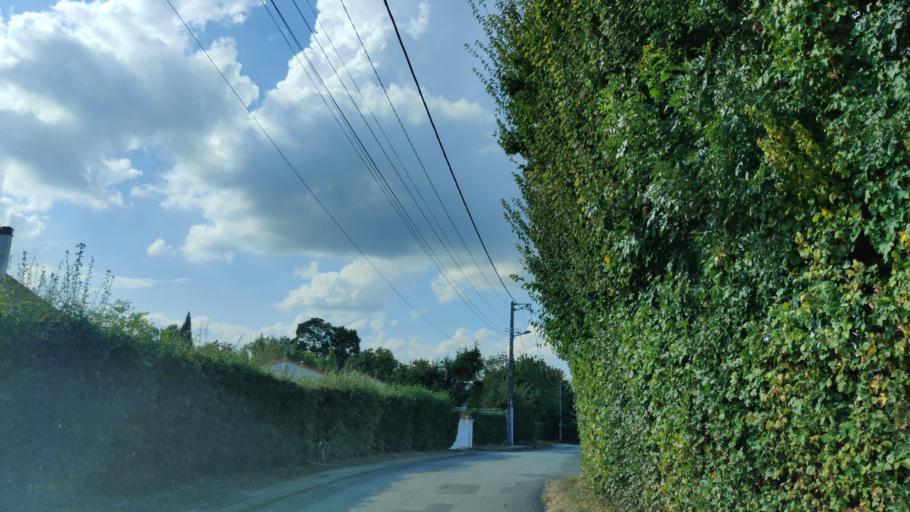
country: FR
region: Poitou-Charentes
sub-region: Departement des Deux-Sevres
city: Bessines
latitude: 46.2996
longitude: -0.5054
